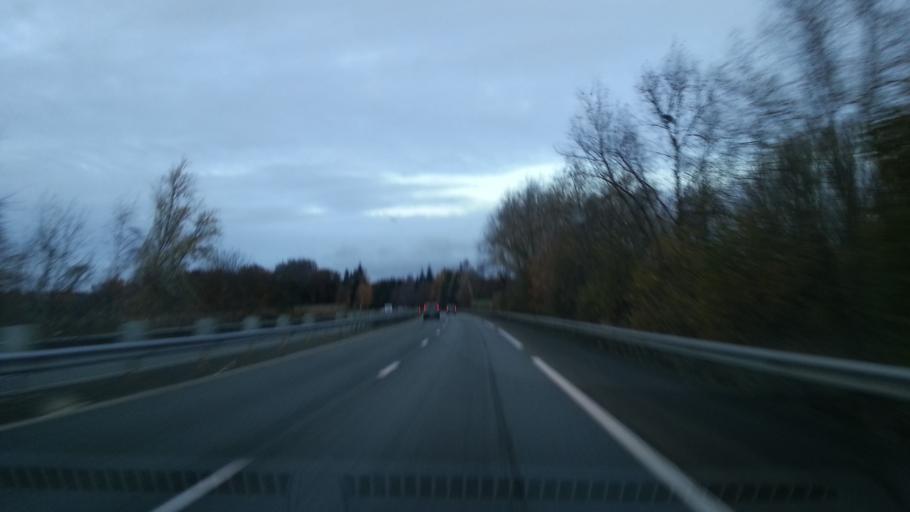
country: FR
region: Picardie
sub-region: Departement de l'Oise
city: Agnetz
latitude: 49.4013
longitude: 2.3721
